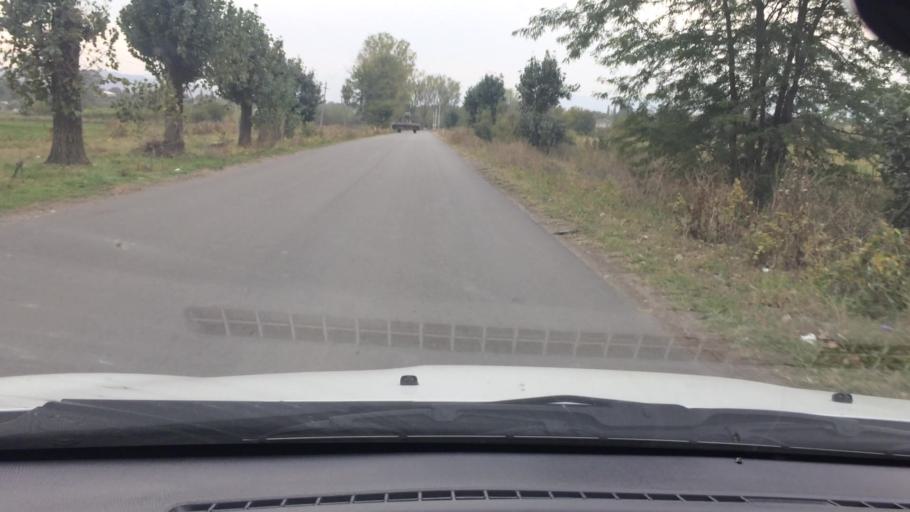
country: AM
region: Tavush
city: Bagratashen
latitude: 41.3352
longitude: 44.9179
